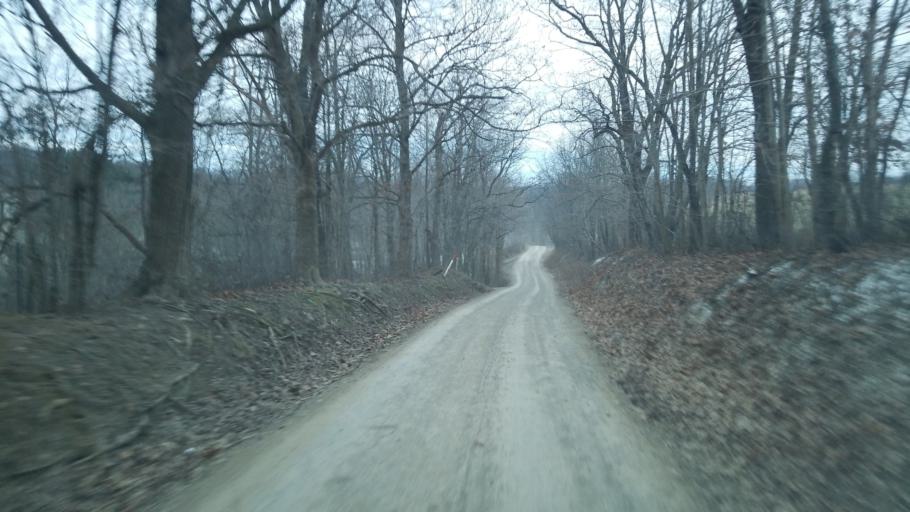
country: US
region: Ohio
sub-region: Holmes County
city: Millersburg
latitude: 40.4568
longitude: -81.8481
